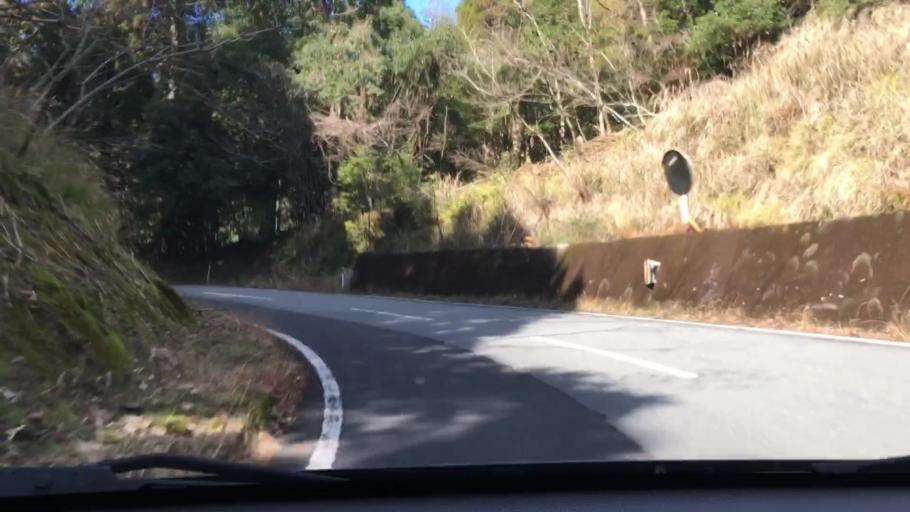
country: JP
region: Kagoshima
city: Ijuin
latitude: 31.7151
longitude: 130.4157
